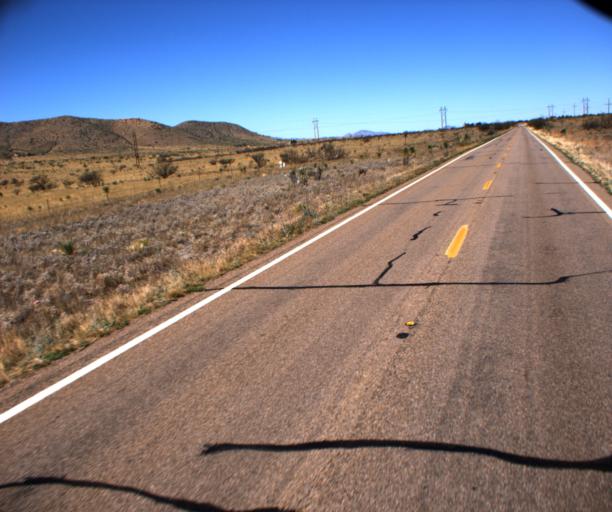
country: US
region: Arizona
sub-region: Cochise County
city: Huachuca City
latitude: 31.7192
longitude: -110.4752
